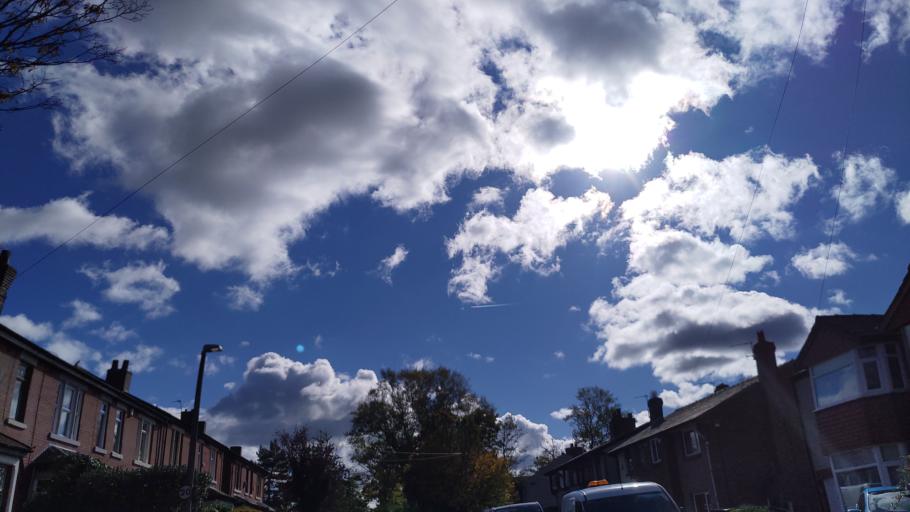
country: GB
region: England
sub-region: Lancashire
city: Chorley
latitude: 53.6575
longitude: -2.6217
